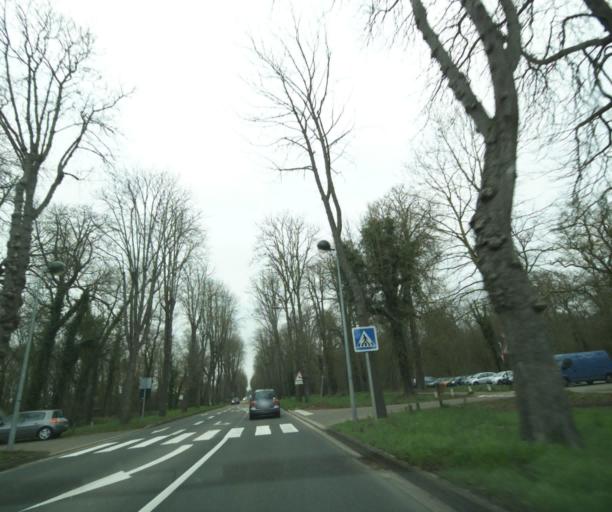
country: FR
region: Ile-de-France
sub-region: Departement des Yvelines
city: Saint-Germain-en-Laye
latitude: 48.9053
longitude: 2.0817
